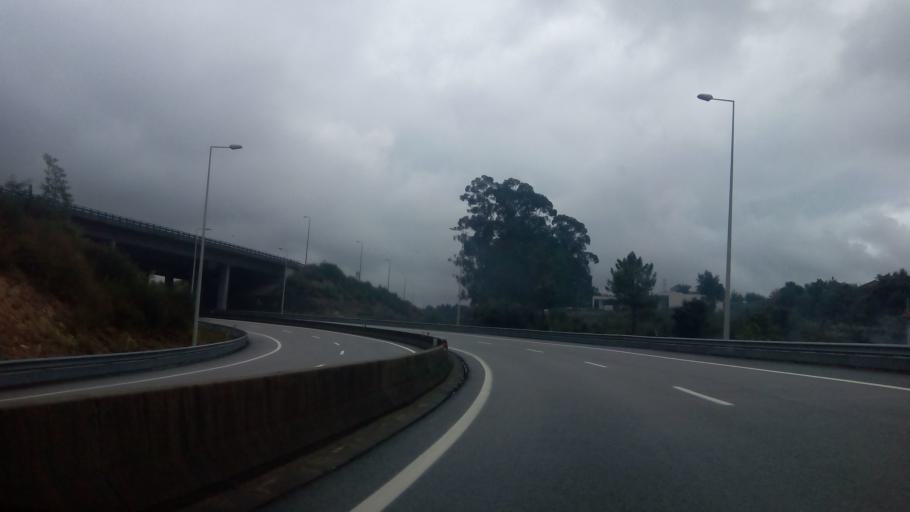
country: PT
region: Porto
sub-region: Valongo
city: Campo
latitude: 41.1823
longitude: -8.4545
